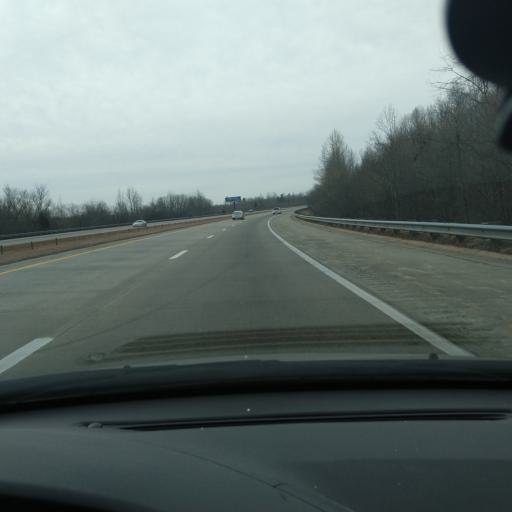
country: US
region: North Carolina
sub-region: Davidson County
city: Welcome
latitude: 35.8804
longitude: -80.2312
